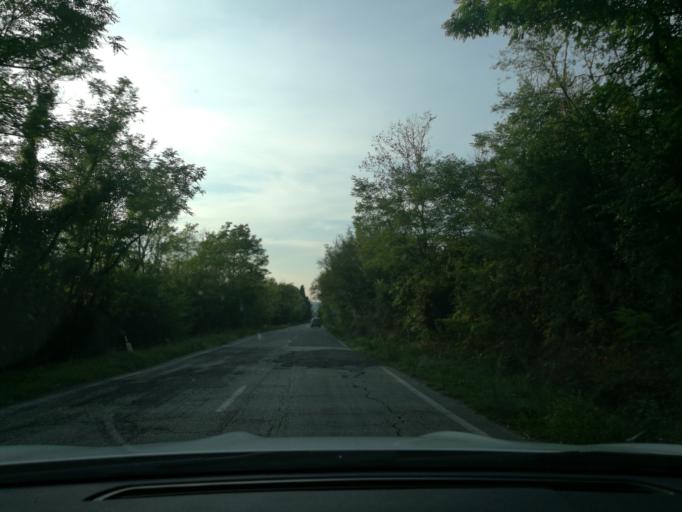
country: IT
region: Umbria
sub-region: Provincia di Terni
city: San Gemini
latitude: 42.6360
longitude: 12.5483
